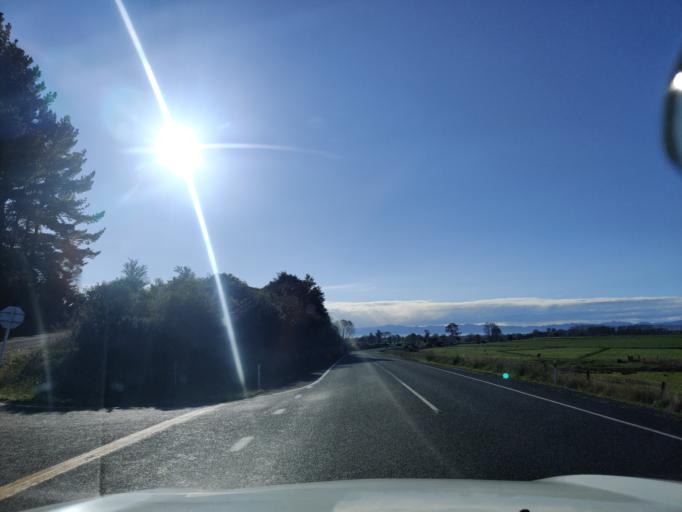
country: NZ
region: Waikato
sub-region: Hauraki District
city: Ngatea
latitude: -37.2829
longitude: 175.4001
